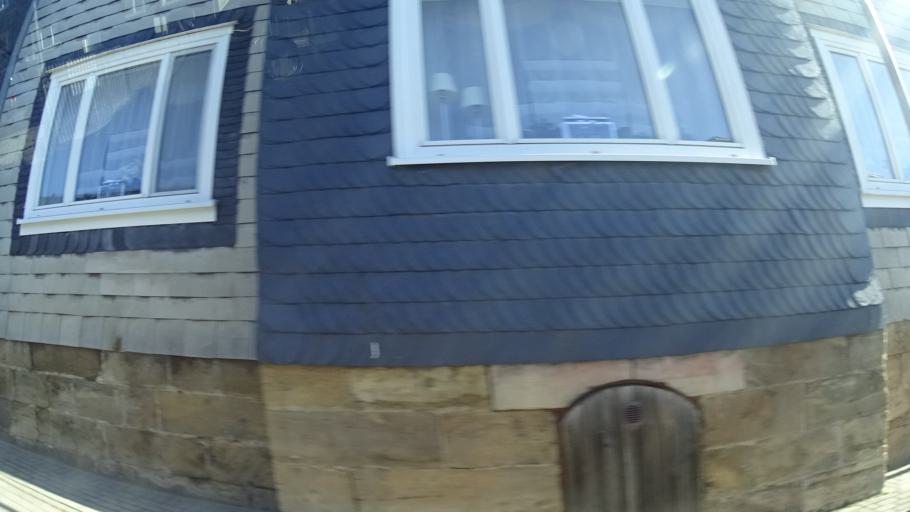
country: DE
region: Thuringia
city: Bohlen
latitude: 50.5874
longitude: 11.0449
